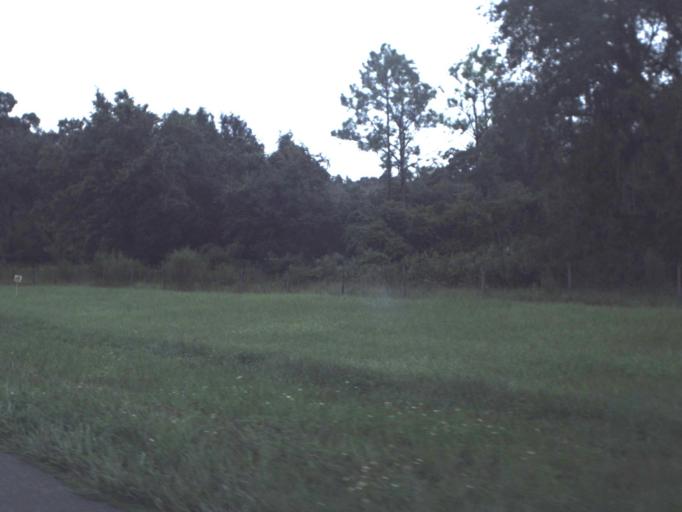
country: US
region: Florida
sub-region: Pasco County
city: Zephyrhills North
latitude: 28.2825
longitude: -82.1174
